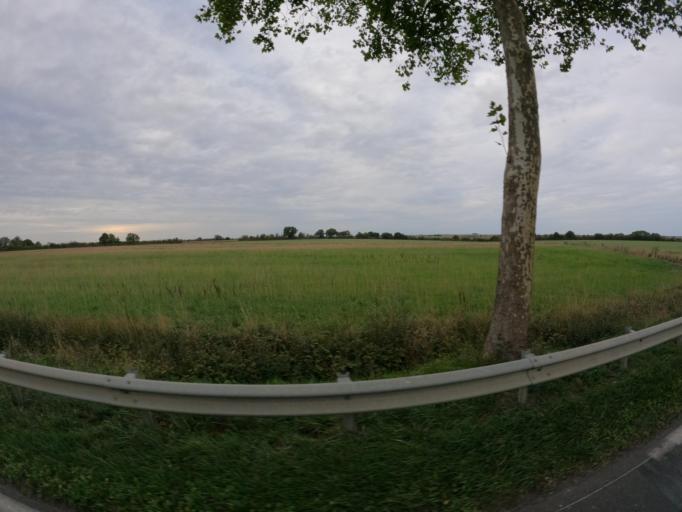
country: FR
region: Poitou-Charentes
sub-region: Departement de la Vienne
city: Ayron
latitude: 46.6605
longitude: 0.0366
